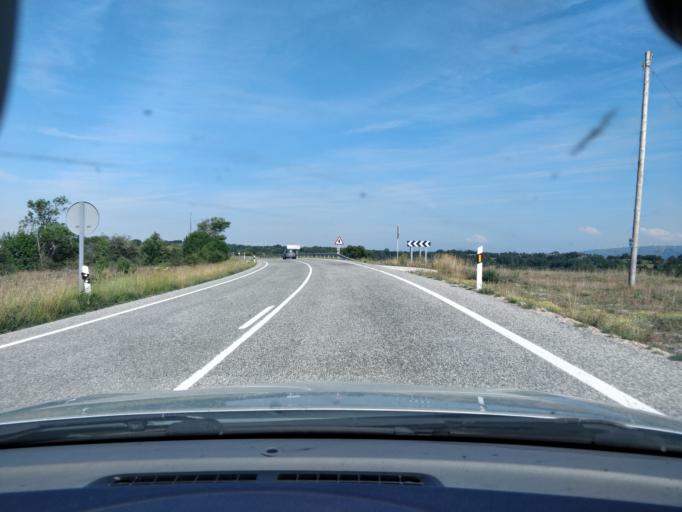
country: ES
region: Cantabria
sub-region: Provincia de Cantabria
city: San Martin de Elines
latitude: 42.9360
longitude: -3.7227
